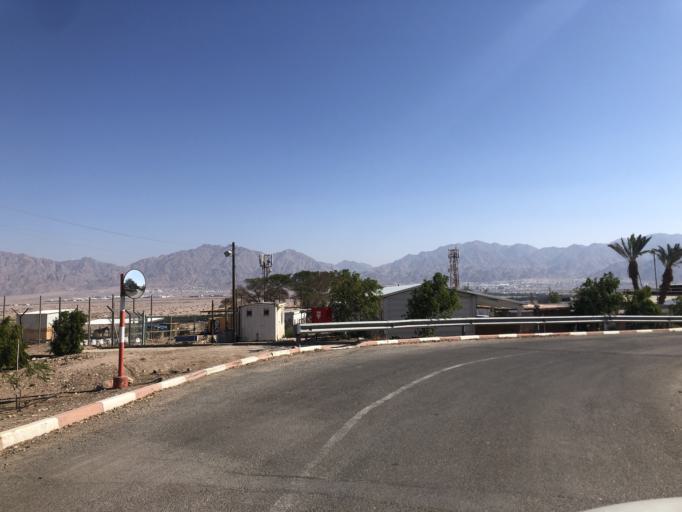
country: IL
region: Southern District
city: Eilat
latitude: 29.5825
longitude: 34.9640
